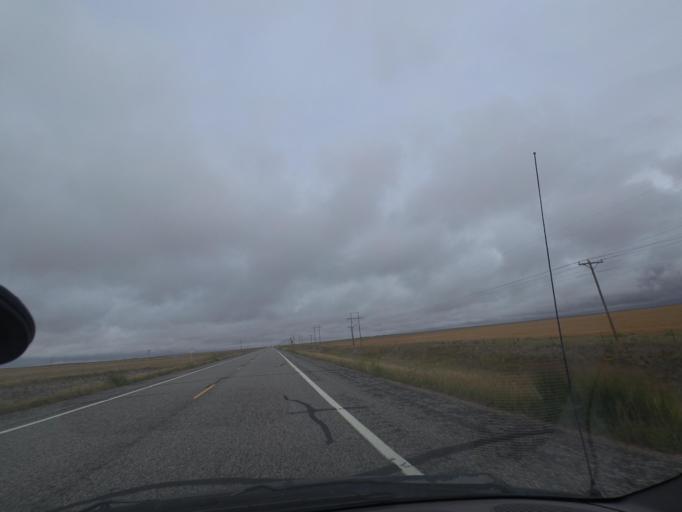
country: US
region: Colorado
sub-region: Washington County
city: Akron
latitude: 39.7395
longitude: -103.3340
